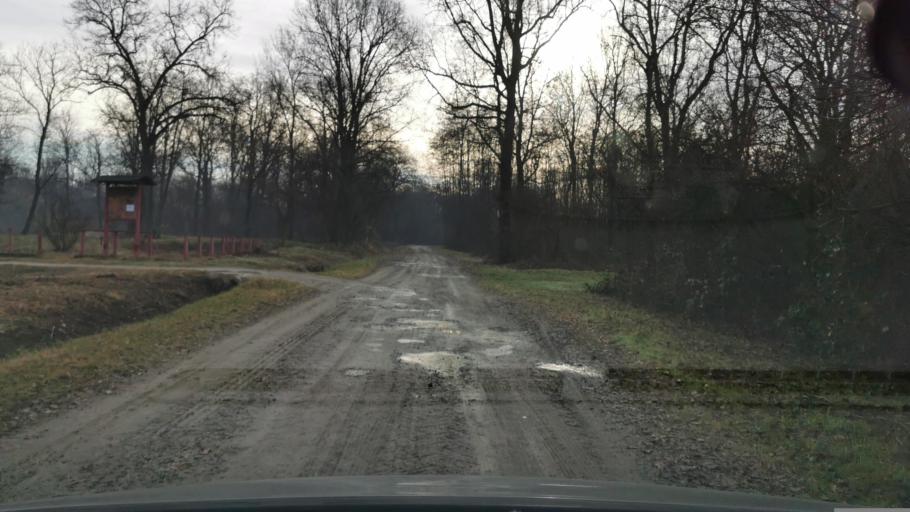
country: IT
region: Piedmont
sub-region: Provincia di Torino
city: Bosconero
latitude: 45.2682
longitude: 7.7824
